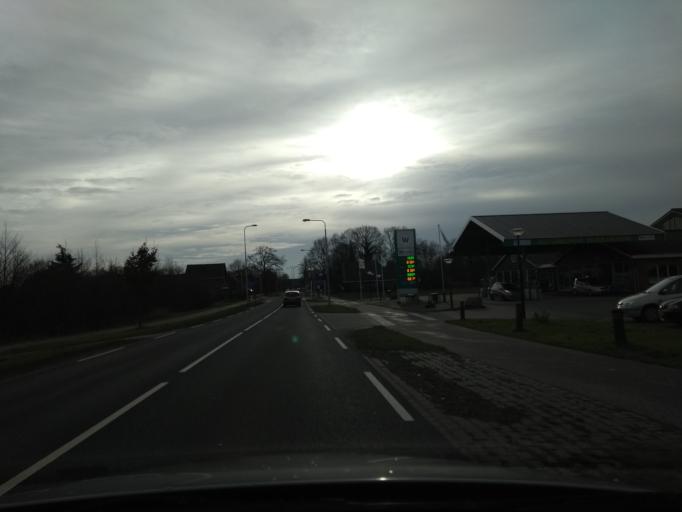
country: NL
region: Overijssel
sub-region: Gemeente Almelo
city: Almelo
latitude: 52.3148
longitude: 6.6551
